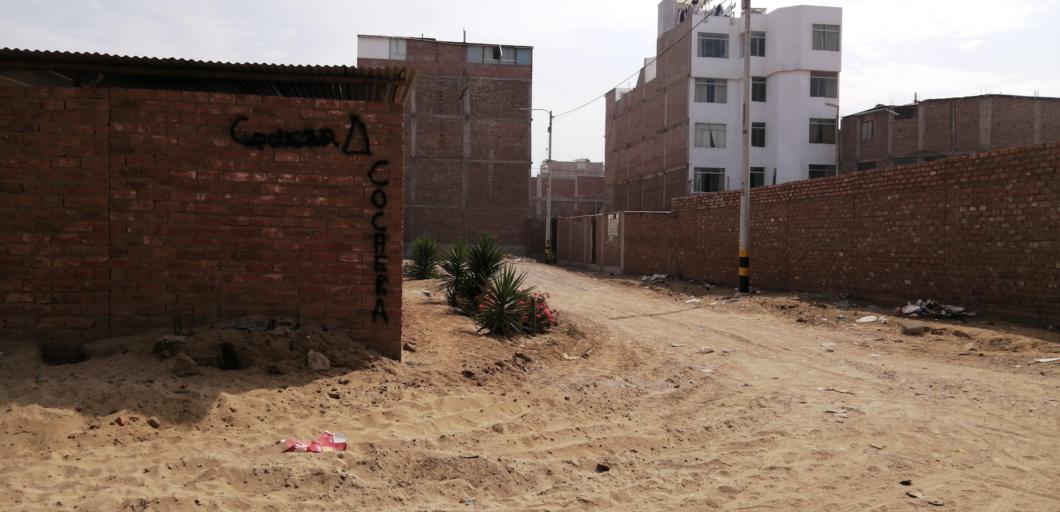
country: PE
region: La Libertad
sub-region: Provincia de Trujillo
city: Trujillo
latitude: -8.1167
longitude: -79.0469
